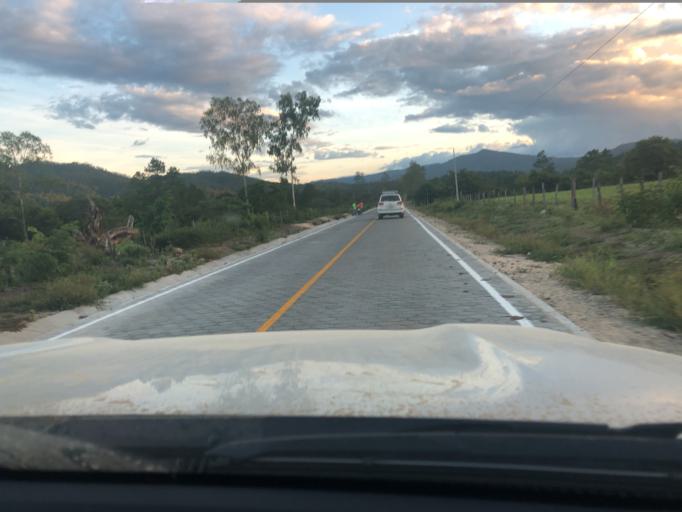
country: HN
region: El Paraiso
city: Santa Cruz
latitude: 13.7226
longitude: -86.6226
